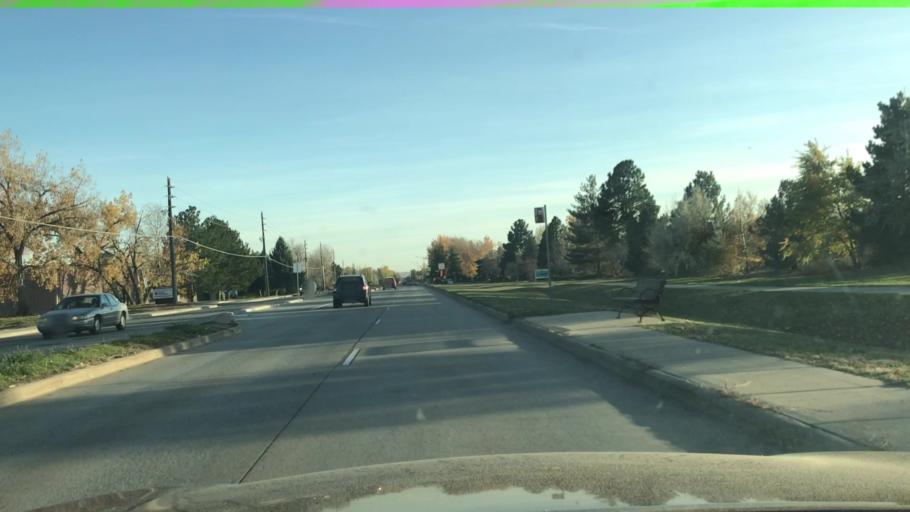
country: US
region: Colorado
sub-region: Boulder County
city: Gunbarrel
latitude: 40.0641
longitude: -105.2069
